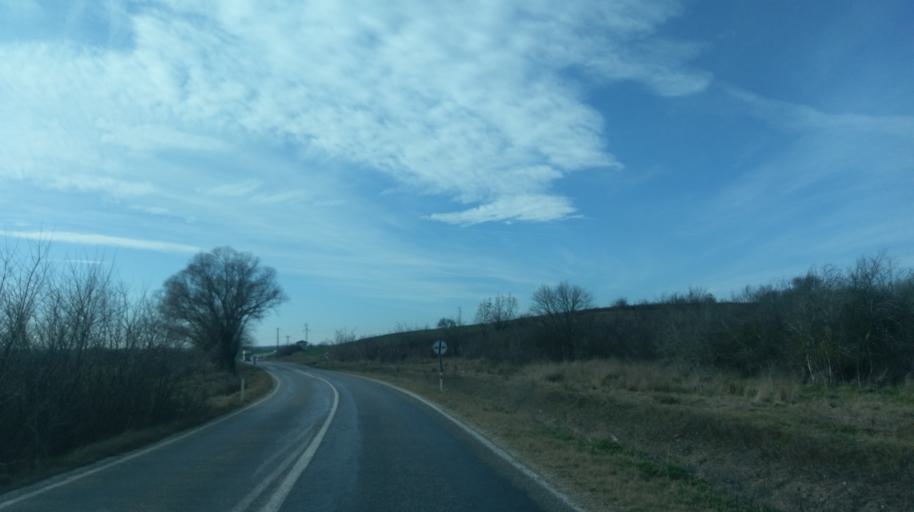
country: TR
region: Kirklareli
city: Pehlivankoy
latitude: 41.3753
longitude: 26.9884
